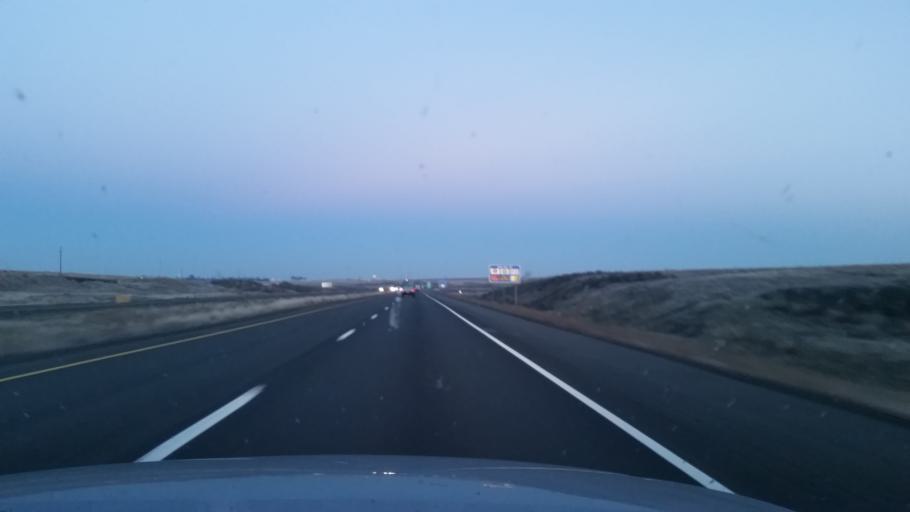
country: US
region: Washington
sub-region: Adams County
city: Ritzville
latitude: 47.1109
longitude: -118.4200
